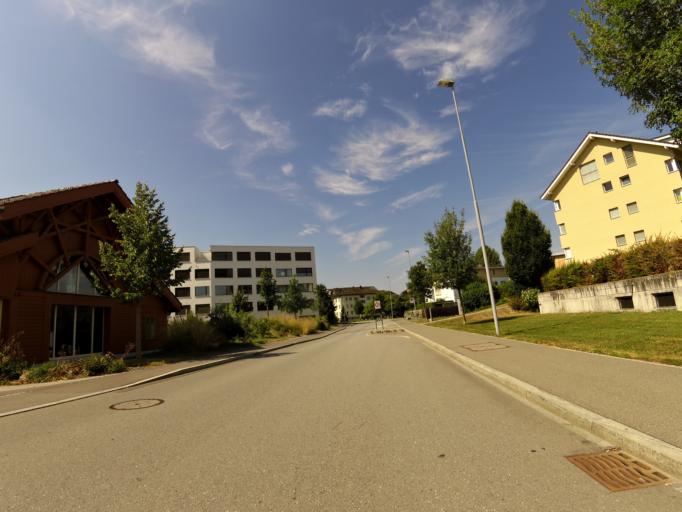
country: CH
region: Lucerne
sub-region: Lucerne-Land District
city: Meierskappel
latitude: 47.1445
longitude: 8.4338
